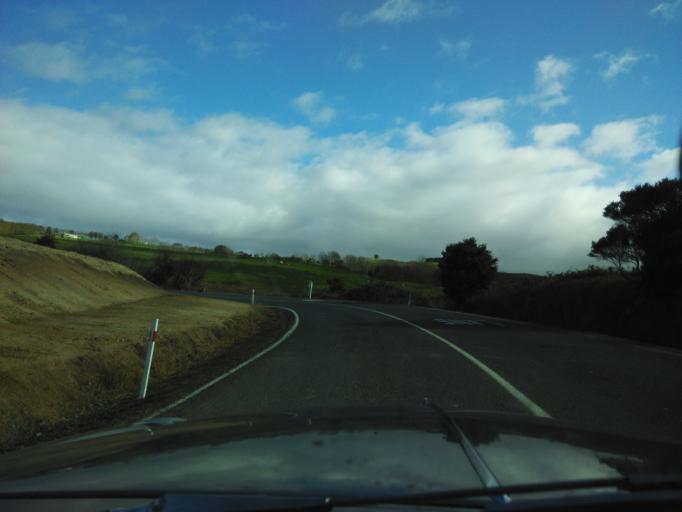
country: NZ
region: Auckland
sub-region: Auckland
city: Wellsford
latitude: -36.1654
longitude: 174.4243
